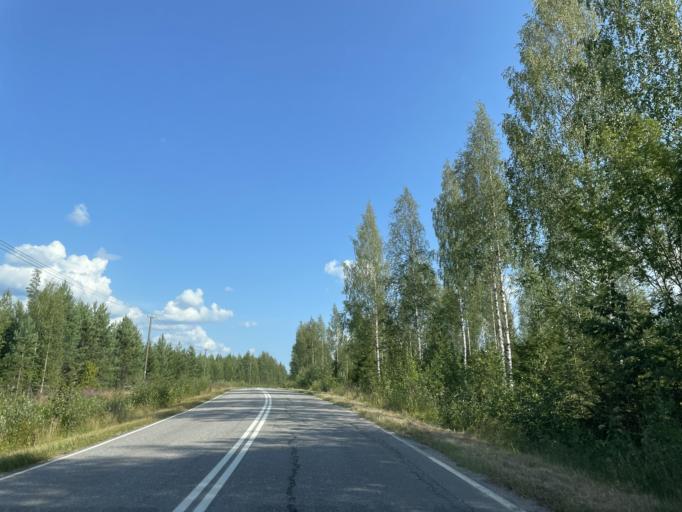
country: FI
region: Central Finland
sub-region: Saarijaervi-Viitasaari
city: Pihtipudas
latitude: 63.3524
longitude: 25.7828
